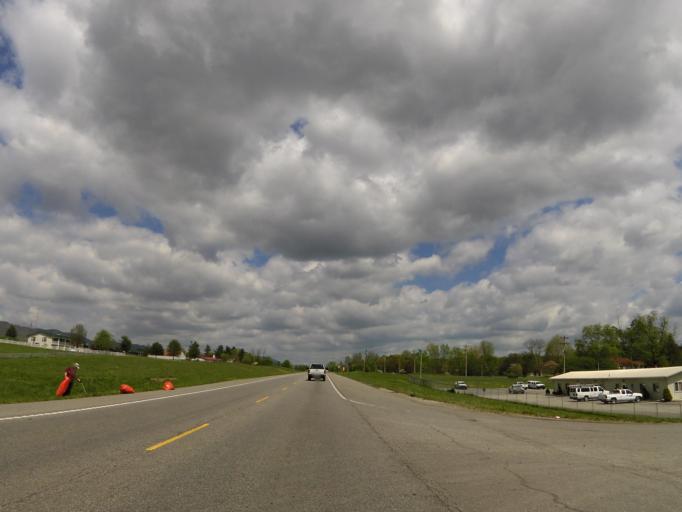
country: US
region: Tennessee
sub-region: Campbell County
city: Fincastle
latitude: 36.4032
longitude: -84.0741
